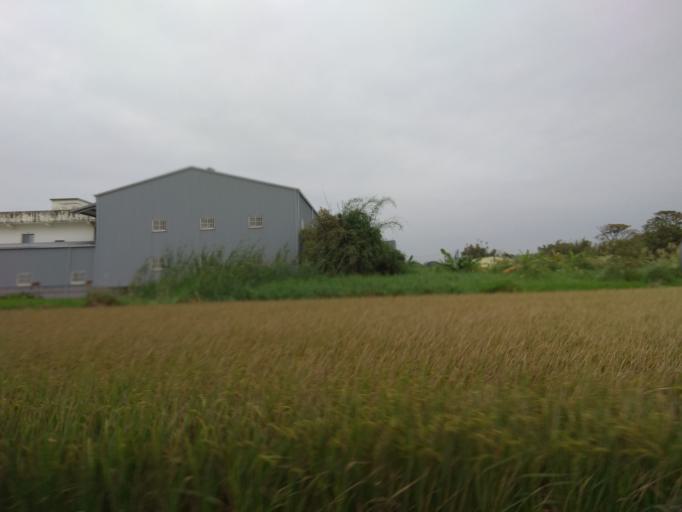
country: TW
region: Taiwan
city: Taoyuan City
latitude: 25.0342
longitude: 121.2254
